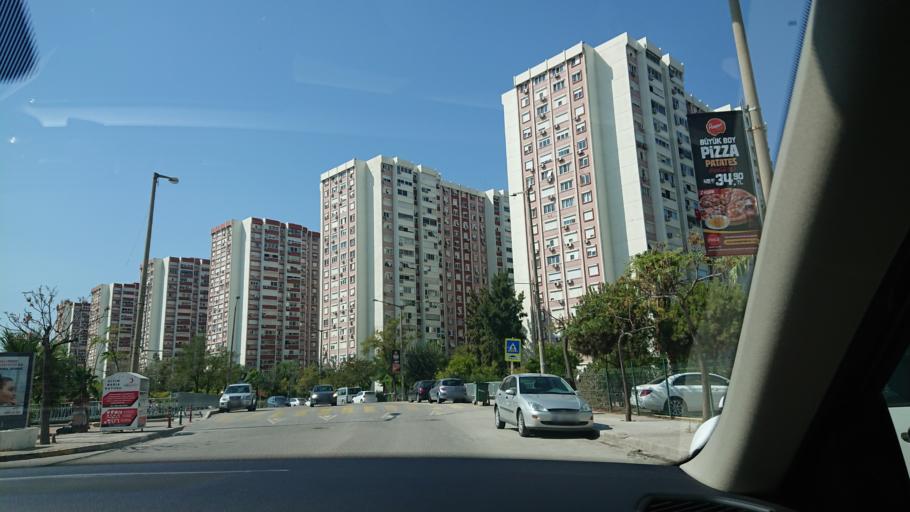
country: TR
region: Izmir
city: Karsiyaka
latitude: 38.4692
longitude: 27.0799
